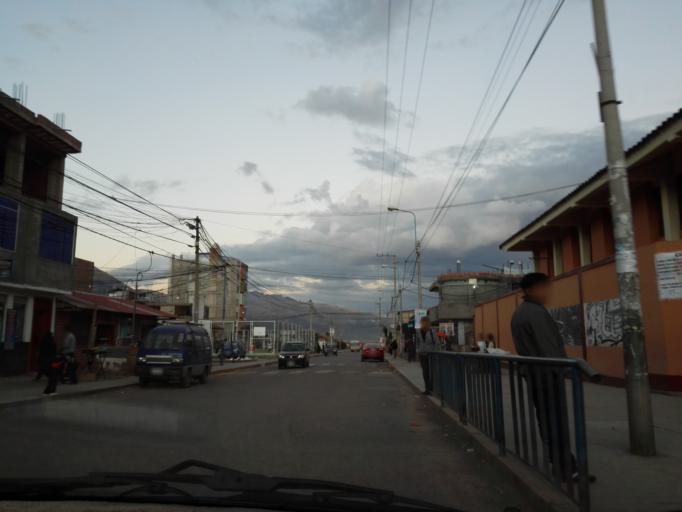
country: PE
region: Cusco
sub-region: Provincia de Cusco
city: Cusco
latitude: -13.5342
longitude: -71.9576
